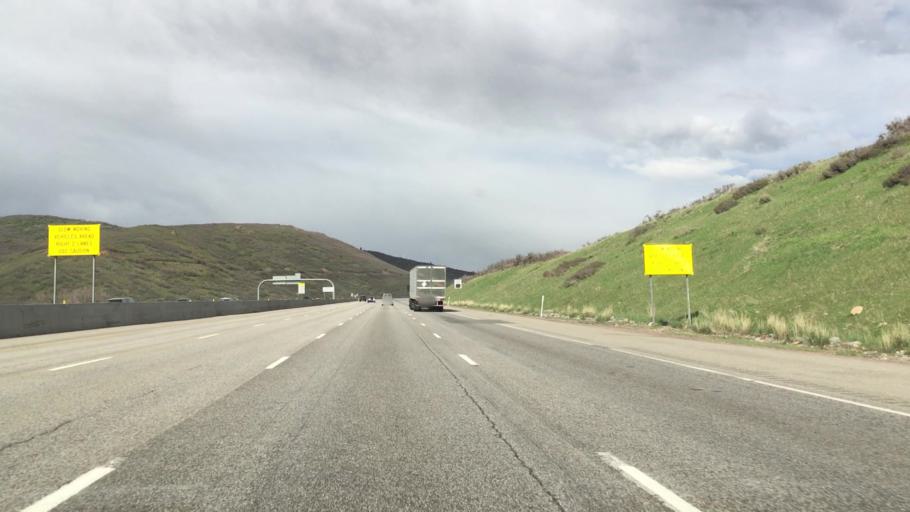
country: US
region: Utah
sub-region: Summit County
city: Summit Park
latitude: 40.7402
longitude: -111.6658
